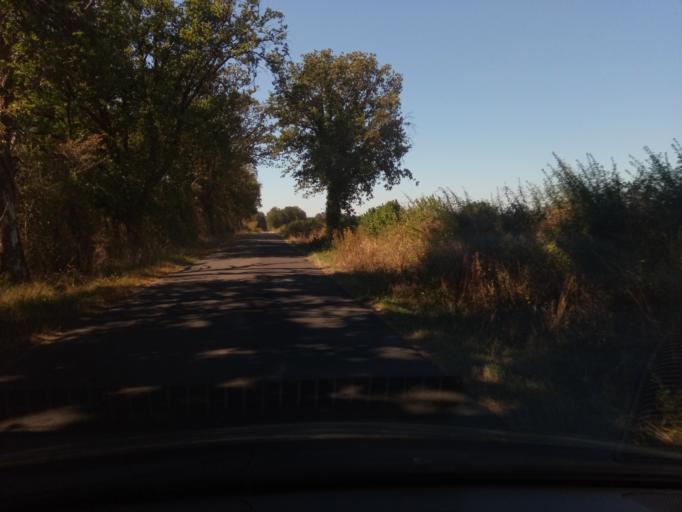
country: FR
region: Poitou-Charentes
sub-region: Departement de la Vienne
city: Montmorillon
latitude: 46.4806
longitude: 0.8615
